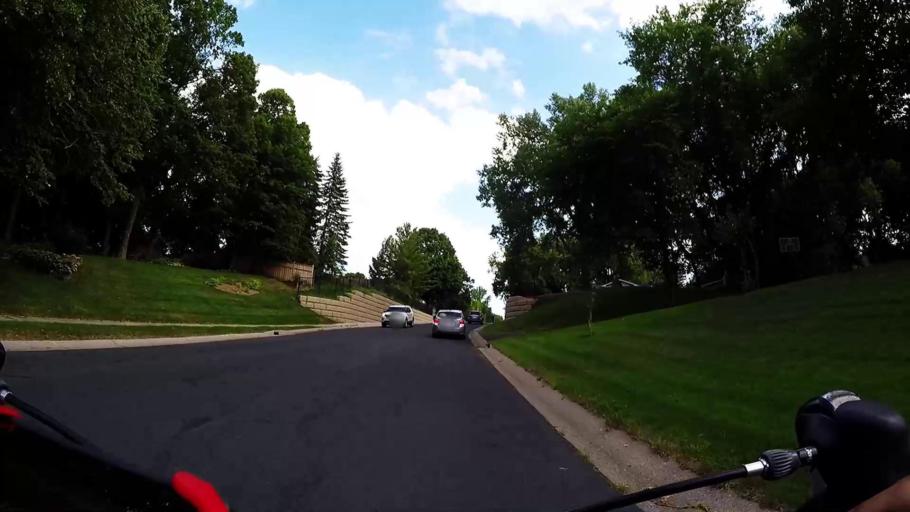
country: US
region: Minnesota
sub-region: Hennepin County
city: Minnetonka
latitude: 44.8879
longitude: -93.4908
